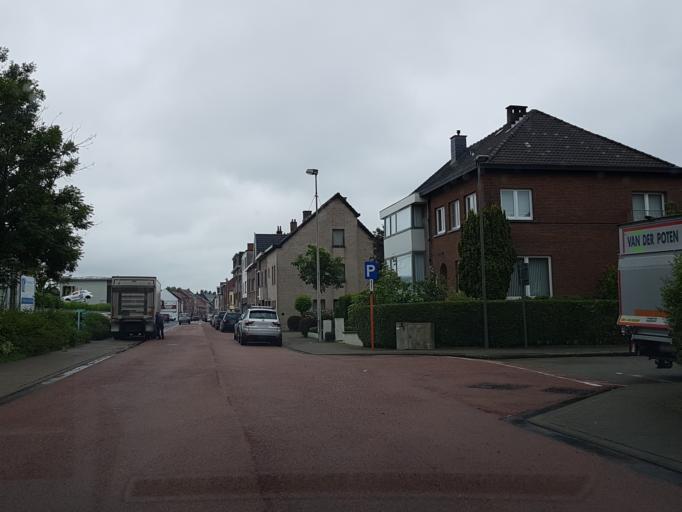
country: BE
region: Flanders
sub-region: Provincie Oost-Vlaanderen
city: Aalst
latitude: 50.9415
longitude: 4.0207
